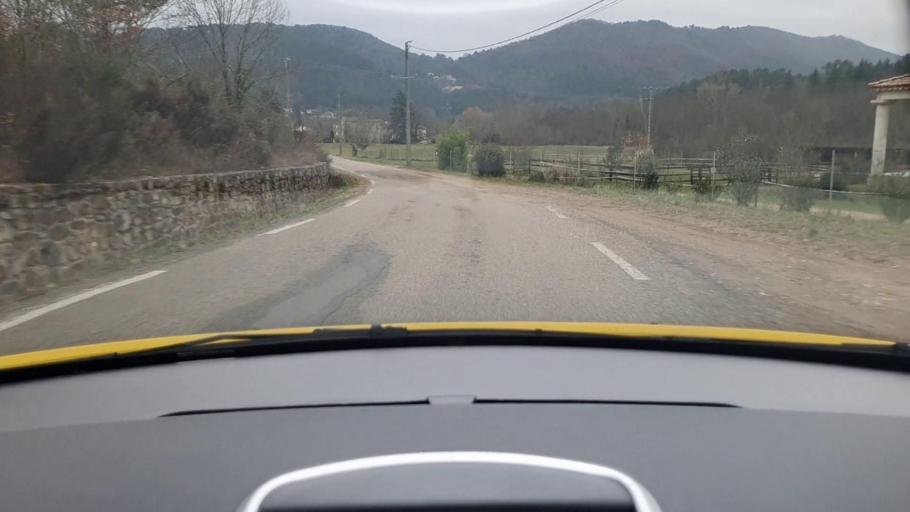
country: FR
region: Languedoc-Roussillon
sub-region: Departement du Gard
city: Besseges
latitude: 44.3216
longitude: 4.1239
